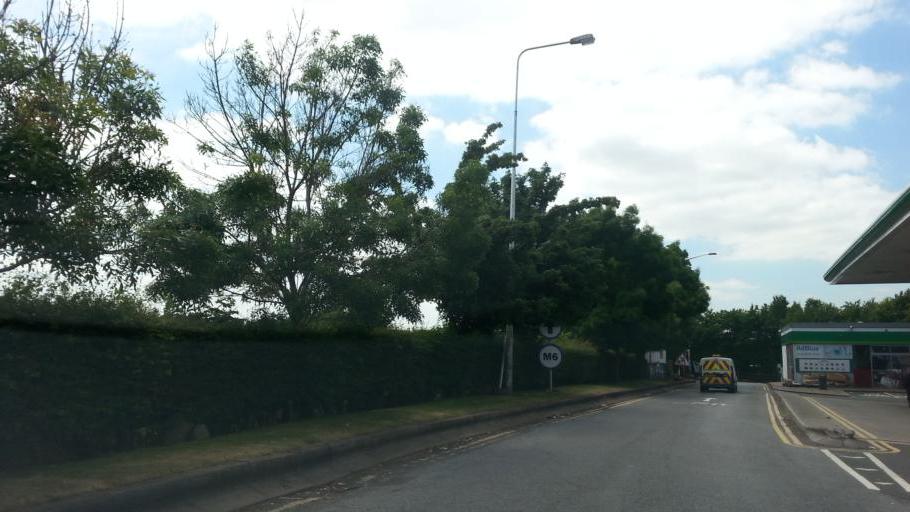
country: GB
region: England
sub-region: Cheshire East
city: Knutsford
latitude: 53.3007
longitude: -2.3998
